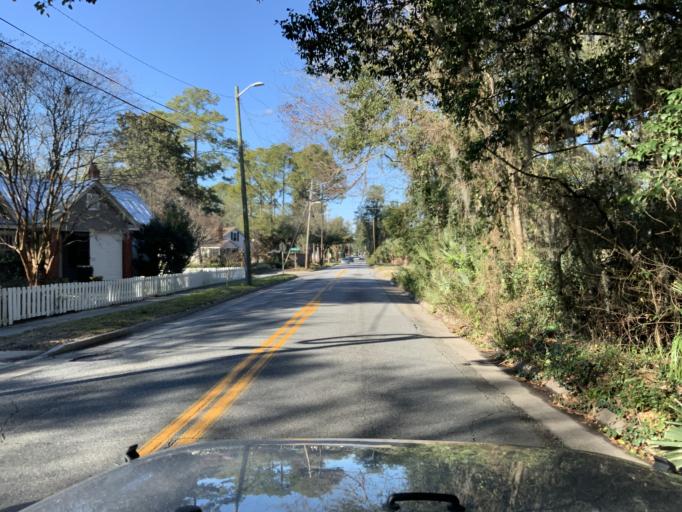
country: US
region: Georgia
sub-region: Chatham County
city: Thunderbolt
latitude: 32.0569
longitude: -81.0688
